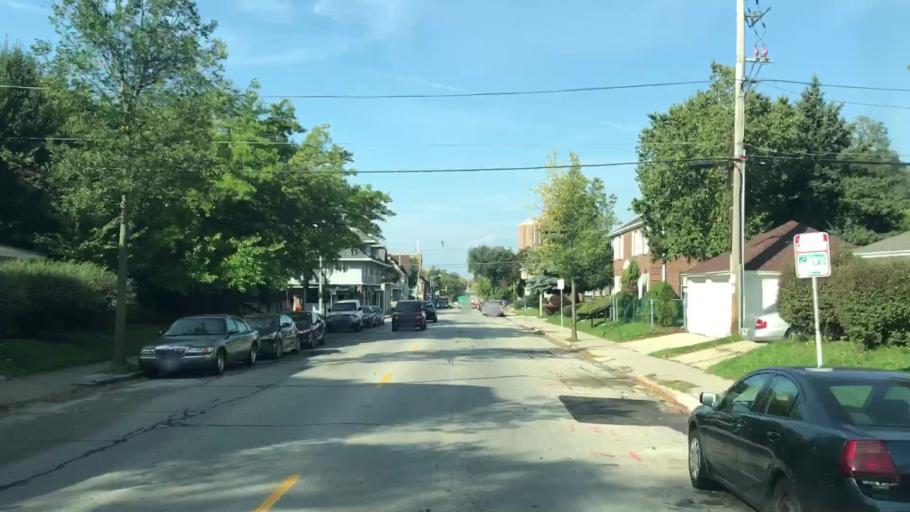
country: US
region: Wisconsin
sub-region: Milwaukee County
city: Shorewood
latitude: 43.0711
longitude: -87.8845
